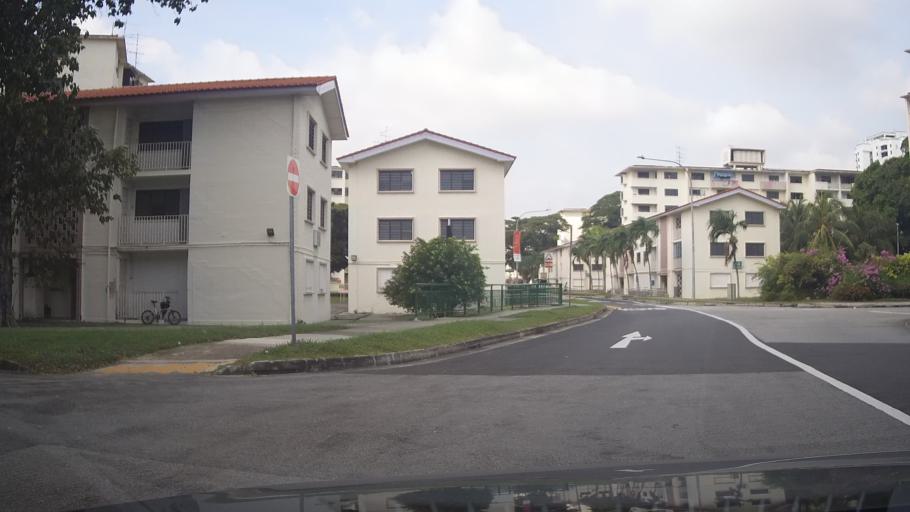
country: SG
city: Singapore
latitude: 1.3064
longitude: 103.8863
